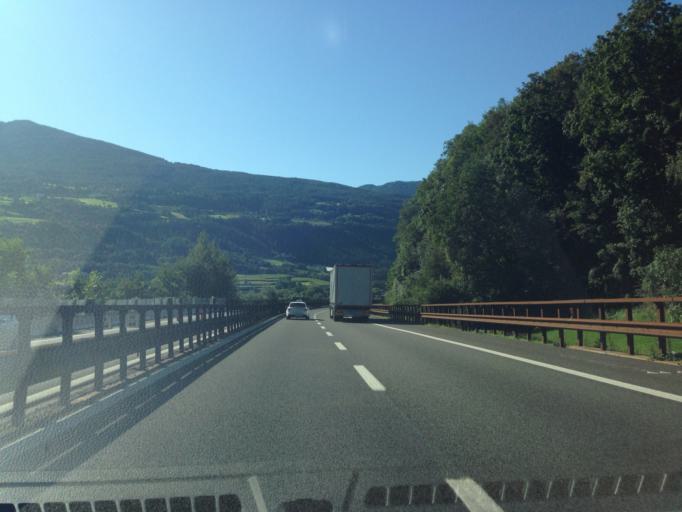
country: IT
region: Trentino-Alto Adige
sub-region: Bolzano
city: Bressanone
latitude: 46.7090
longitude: 11.6482
